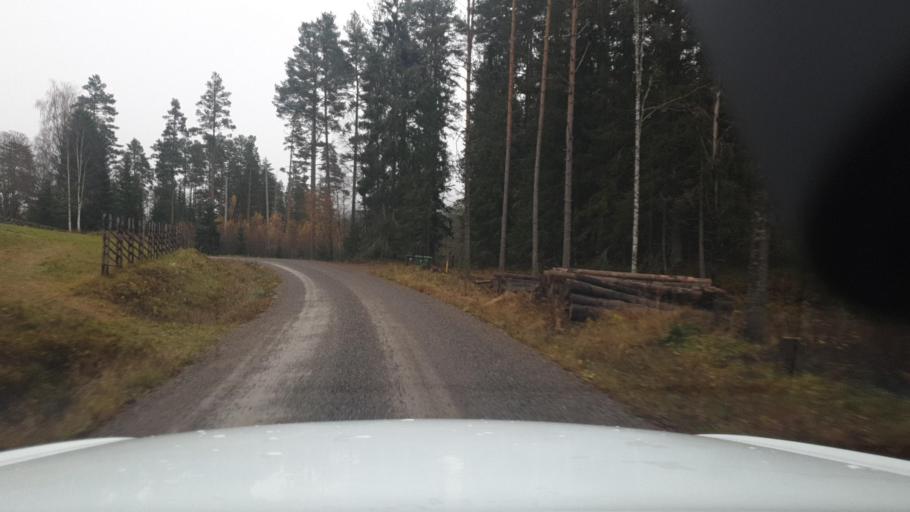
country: SE
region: Vaermland
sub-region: Eda Kommun
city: Charlottenberg
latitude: 60.0211
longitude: 12.6327
